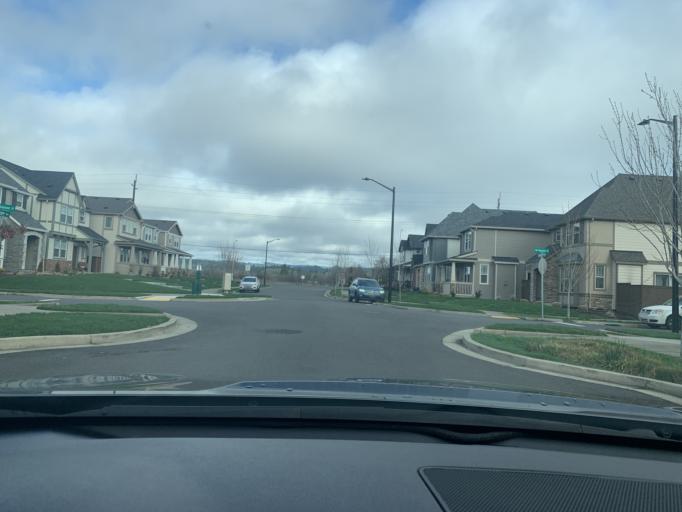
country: US
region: Oregon
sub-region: Washington County
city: North Plains
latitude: 45.5953
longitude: -122.9743
